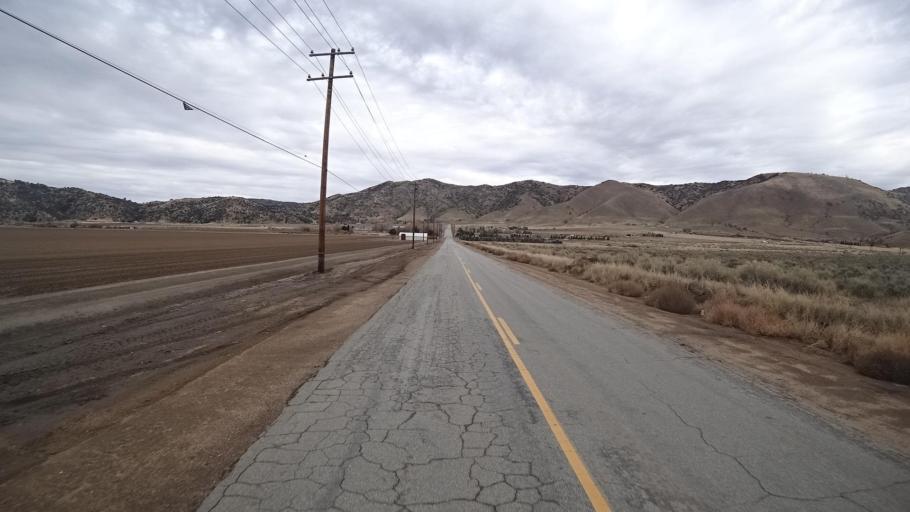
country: US
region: California
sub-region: Kern County
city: Bear Valley Springs
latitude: 35.1276
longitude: -118.5744
